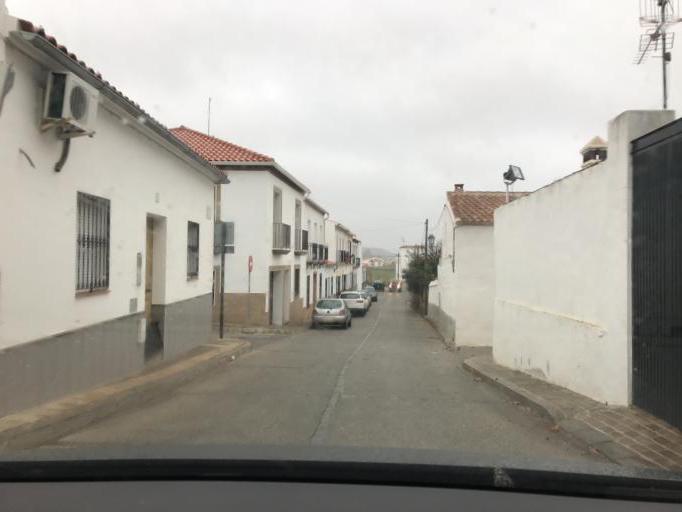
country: ES
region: Andalusia
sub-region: Provincia de Sevilla
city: Guadalcanal
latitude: 38.0950
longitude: -5.8160
